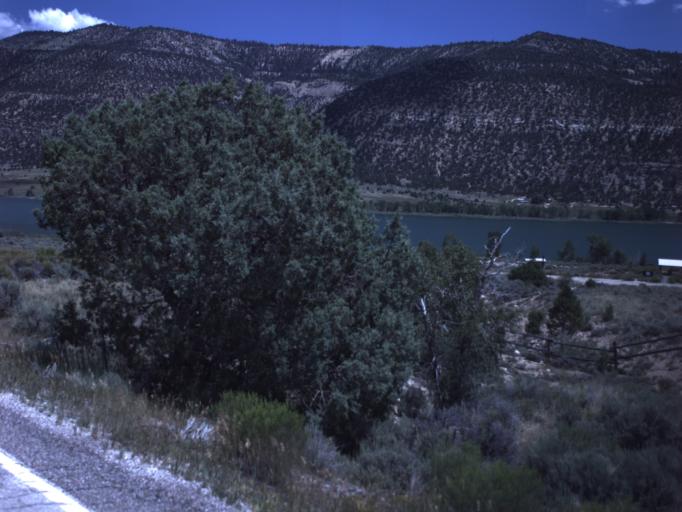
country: US
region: Utah
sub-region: Emery County
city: Orangeville
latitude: 39.3061
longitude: -111.2892
